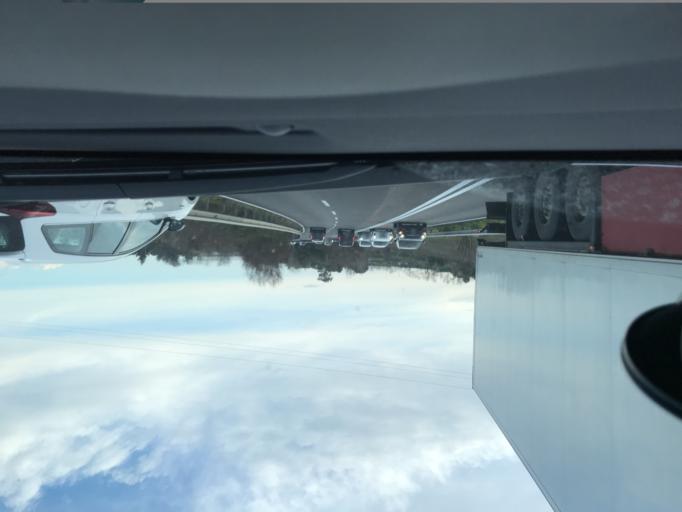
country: IT
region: The Marches
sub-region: Provincia di Ancona
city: Posatora
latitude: 43.5971
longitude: 13.4398
